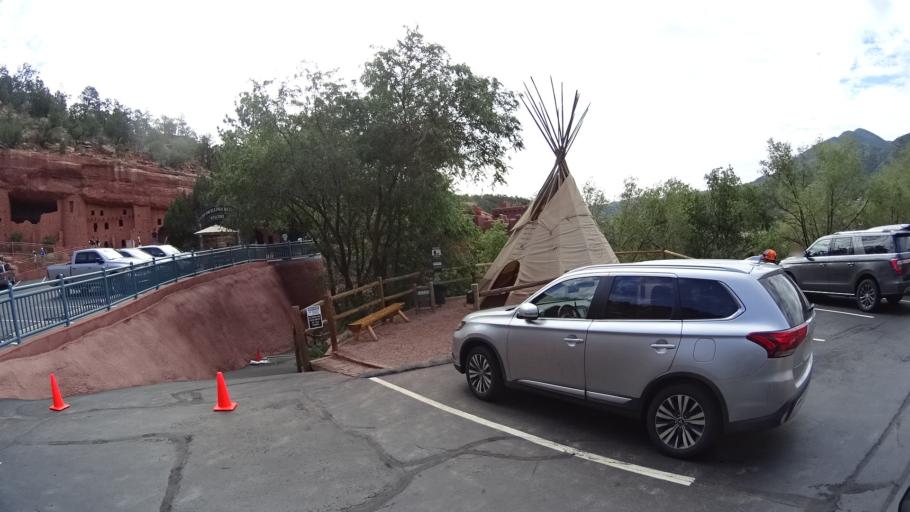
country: US
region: Colorado
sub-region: El Paso County
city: Manitou Springs
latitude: 38.8631
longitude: -104.9128
